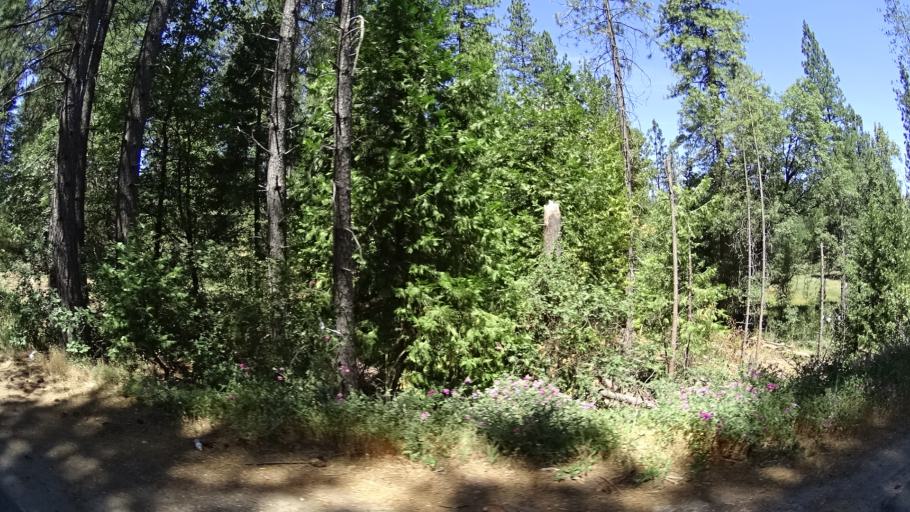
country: US
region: California
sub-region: Amador County
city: Pioneer
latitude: 38.4055
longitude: -120.5192
